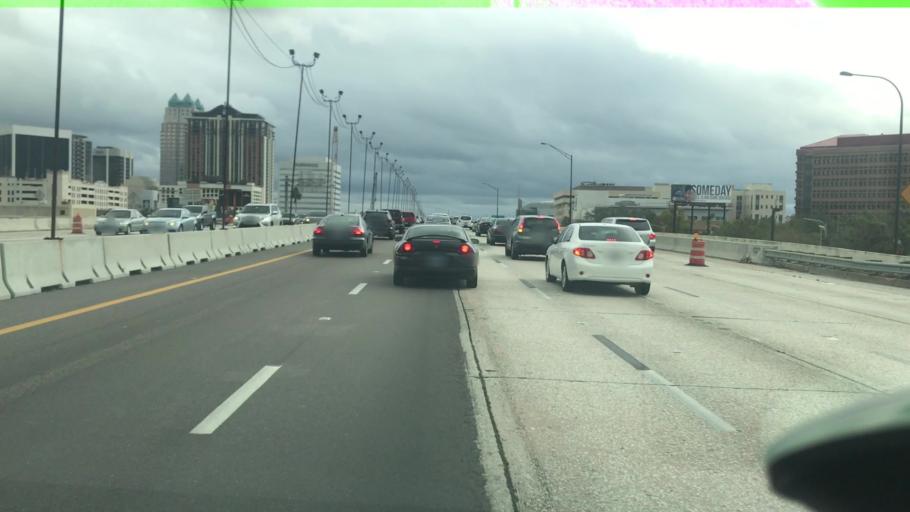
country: US
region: Florida
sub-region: Orange County
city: Orlando
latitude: 28.5480
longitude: -81.3826
